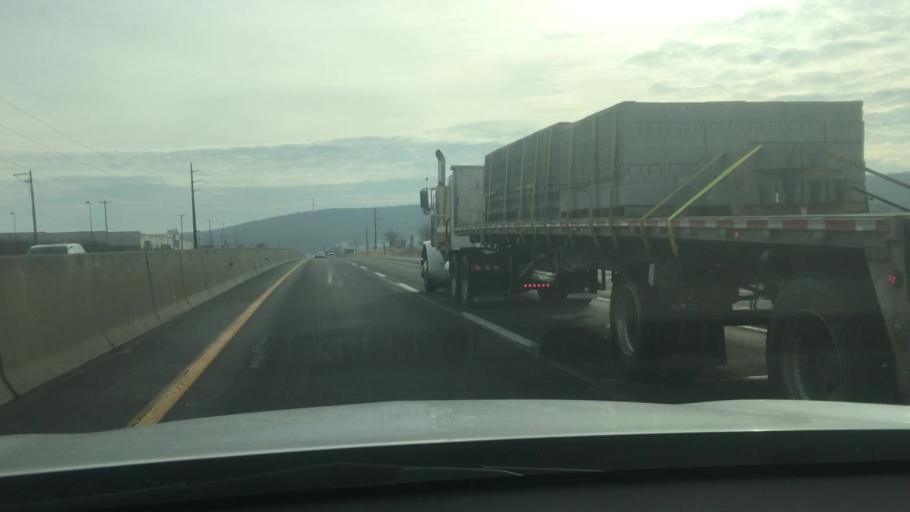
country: US
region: Pennsylvania
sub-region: Chester County
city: Elverson
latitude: 40.1555
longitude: -75.8713
